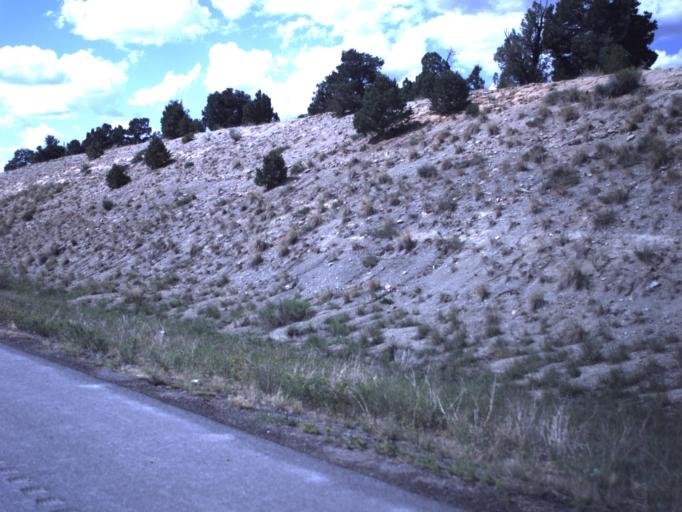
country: US
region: Utah
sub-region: Duchesne County
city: Duchesne
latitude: 40.1832
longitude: -110.6611
